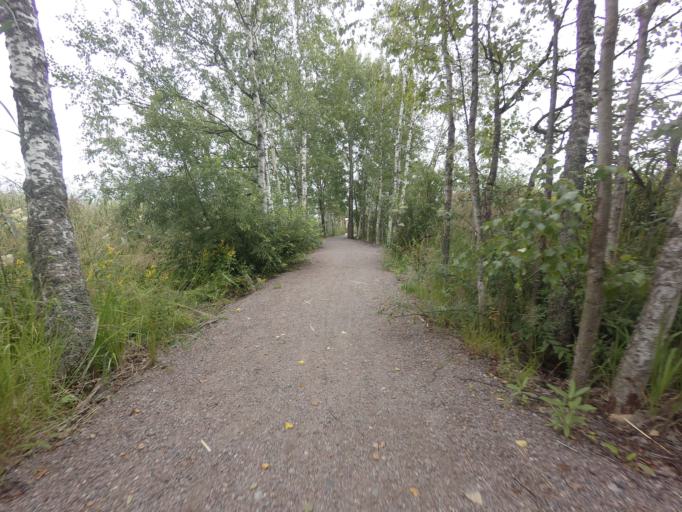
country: FI
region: Uusimaa
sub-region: Helsinki
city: Otaniemi
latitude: 60.1893
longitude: 24.8180
